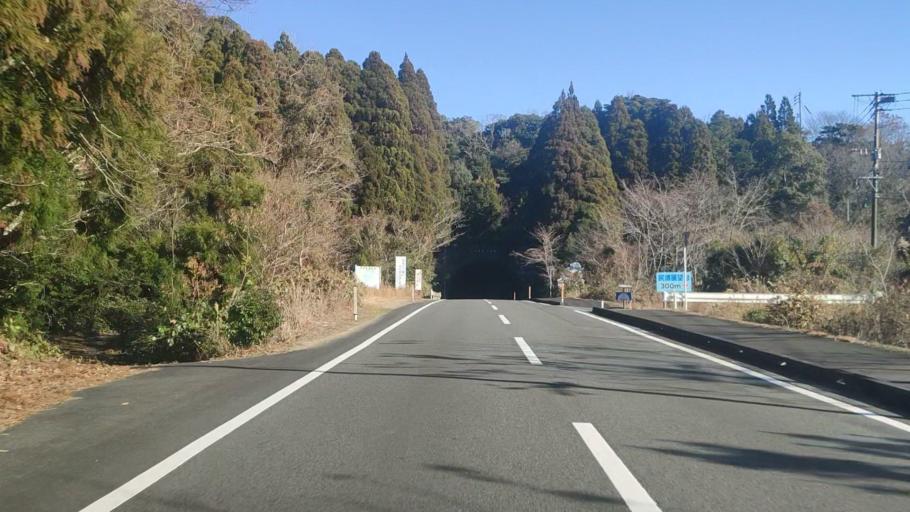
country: JP
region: Miyazaki
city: Nobeoka
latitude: 32.6971
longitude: 131.8130
